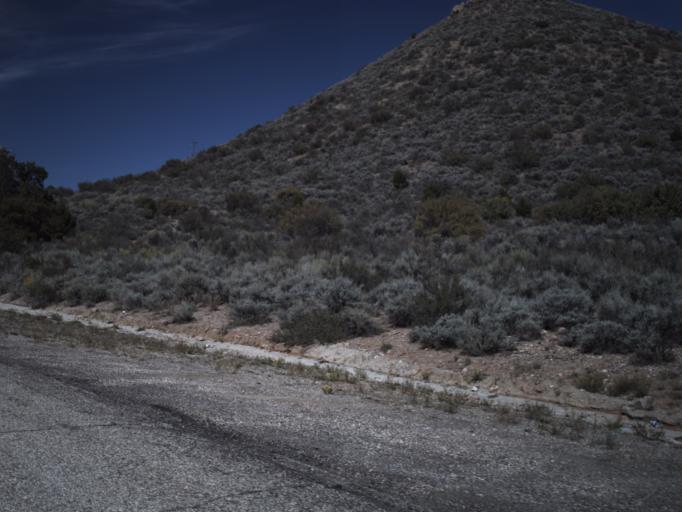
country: US
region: Utah
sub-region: Washington County
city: Enterprise
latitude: 37.4635
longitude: -113.6342
